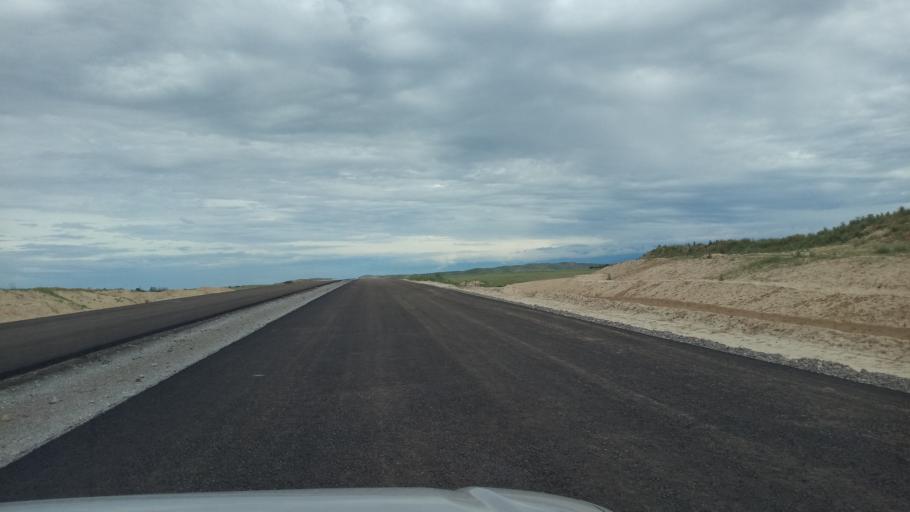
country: KG
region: Chuy
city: Bystrovka
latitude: 43.3008
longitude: 76.1197
